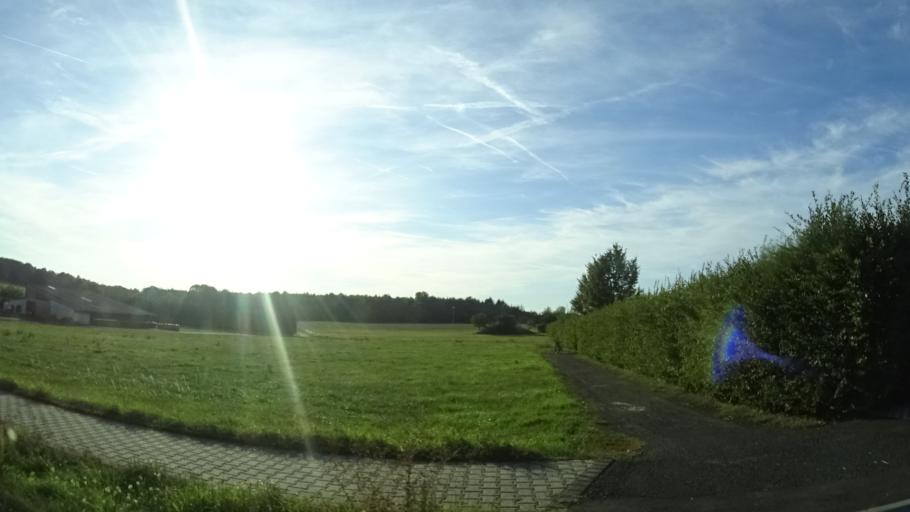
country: DE
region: Hesse
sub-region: Regierungsbezirk Darmstadt
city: Wachtersbach
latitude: 50.2903
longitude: 9.2624
